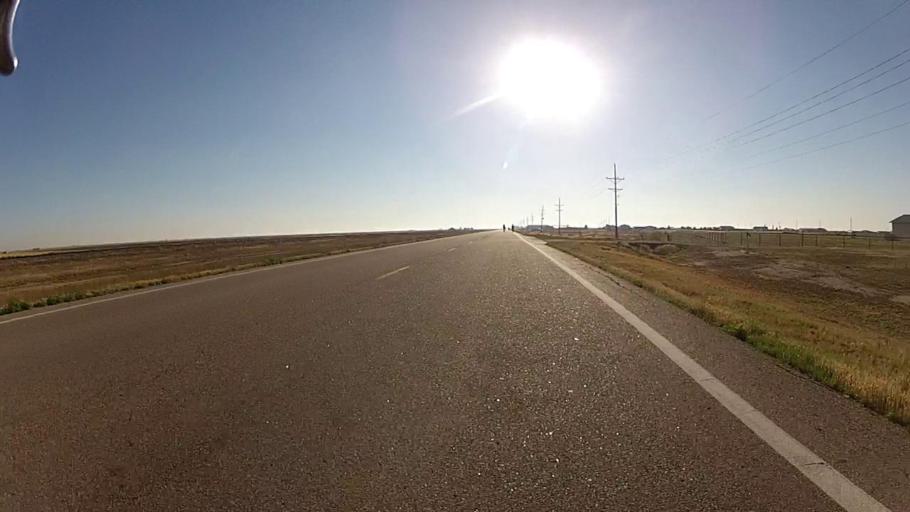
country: US
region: Kansas
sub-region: Haskell County
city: Sublette
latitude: 37.4934
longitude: -100.8079
